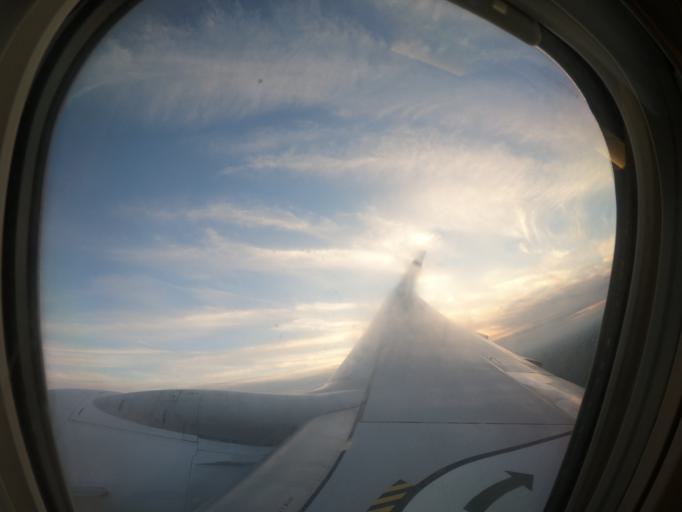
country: GB
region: England
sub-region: Essex
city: Little Hallingbury
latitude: 51.8357
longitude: 0.1933
